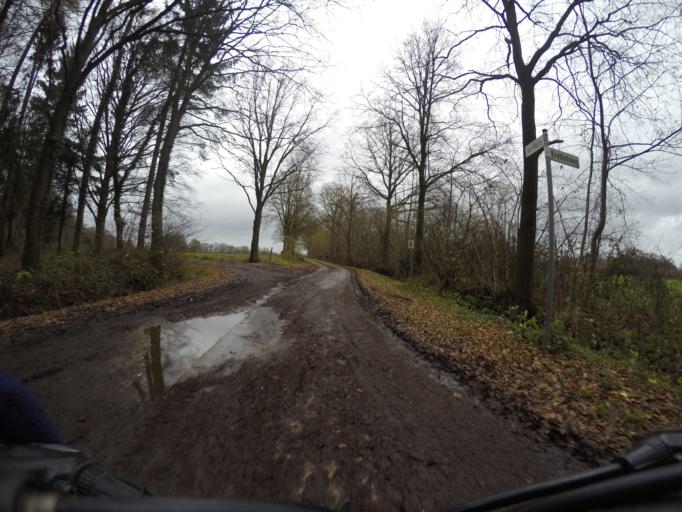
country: DE
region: Schleswig-Holstein
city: Borstel-Hohenraden
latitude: 53.7213
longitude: 9.8315
